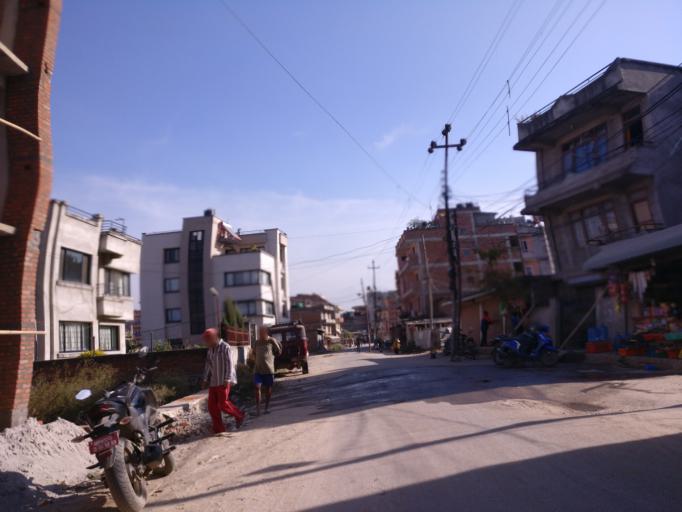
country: NP
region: Central Region
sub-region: Bagmati Zone
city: Patan
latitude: 27.6746
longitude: 85.3332
